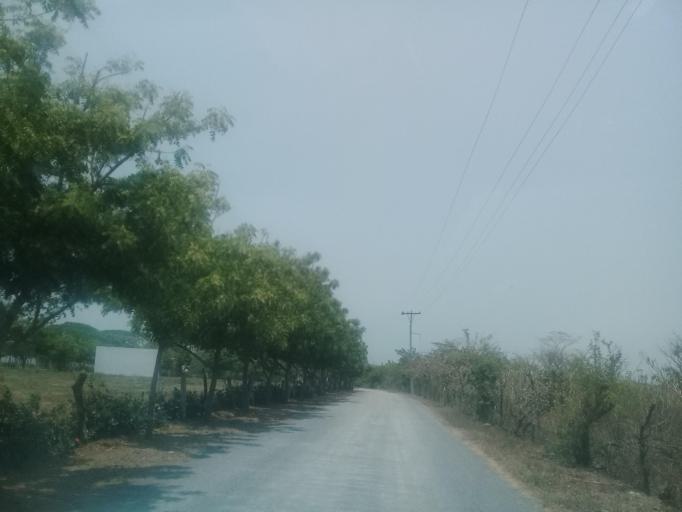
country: MX
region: Veracruz
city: Jamapa
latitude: 19.0857
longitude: -96.2364
